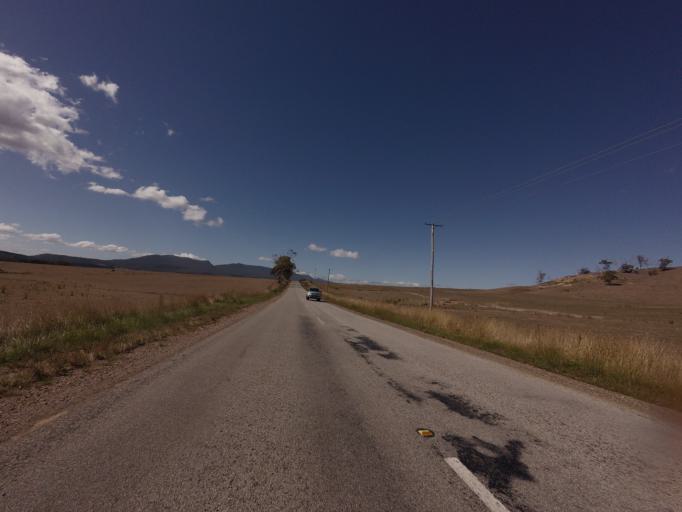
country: AU
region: Tasmania
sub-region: Break O'Day
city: St Helens
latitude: -41.6137
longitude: 148.0136
